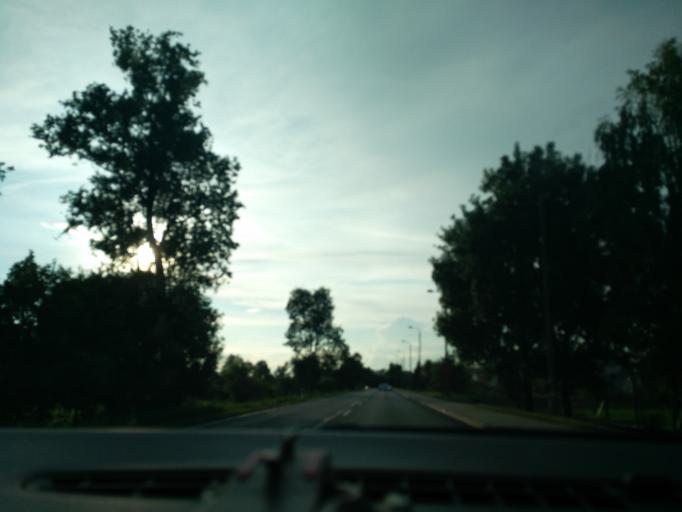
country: PL
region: Lublin Voivodeship
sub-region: Powiat krasnicki
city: Krasnik
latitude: 50.9072
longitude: 22.2660
